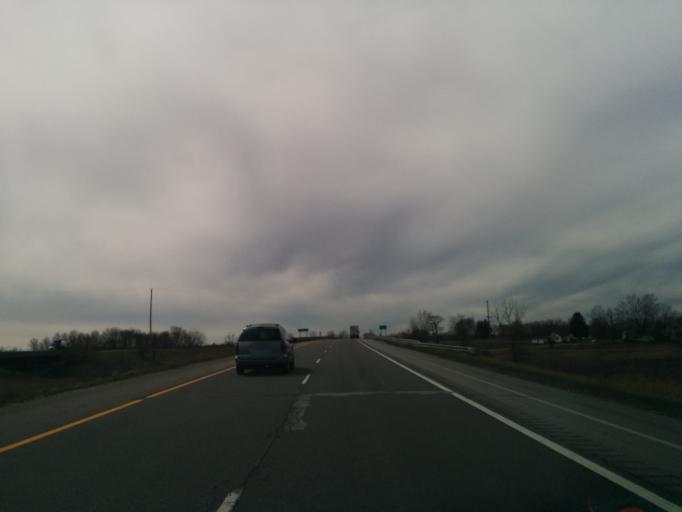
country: US
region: Michigan
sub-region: Ottawa County
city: Zeeland
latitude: 42.7704
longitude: -86.0357
